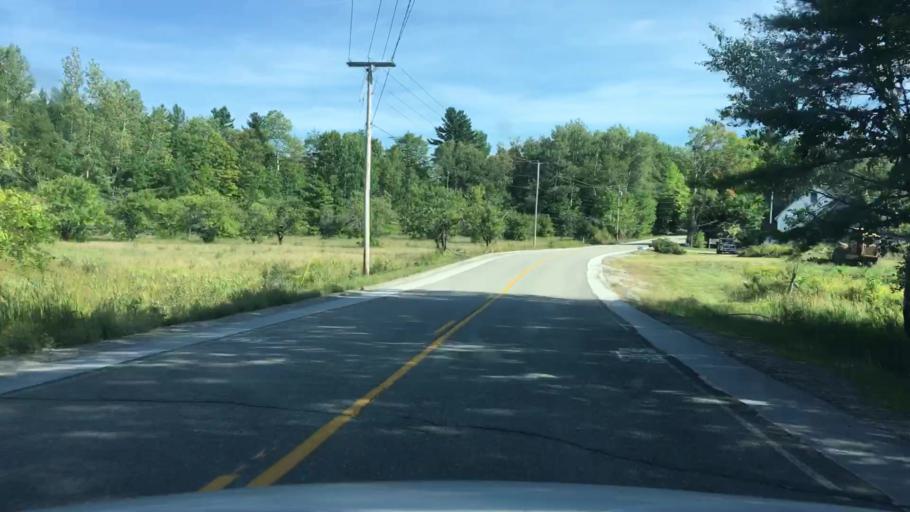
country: US
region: Maine
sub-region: Penobscot County
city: Enfield
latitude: 45.2142
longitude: -68.5272
